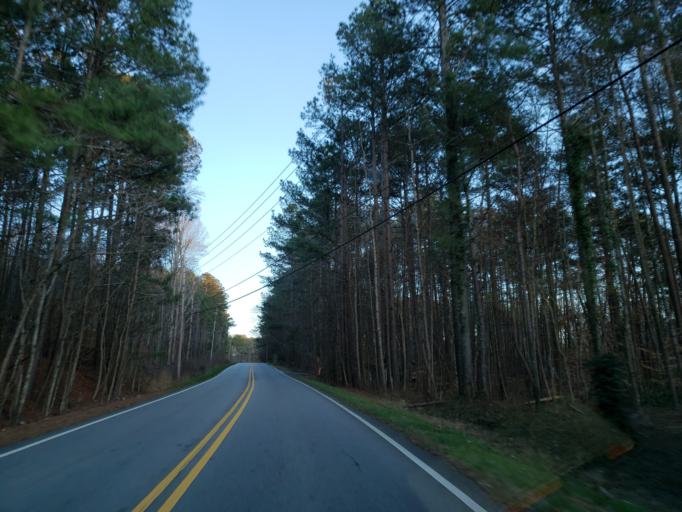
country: US
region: Georgia
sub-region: Cobb County
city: Acworth
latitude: 33.9989
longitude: -84.7329
